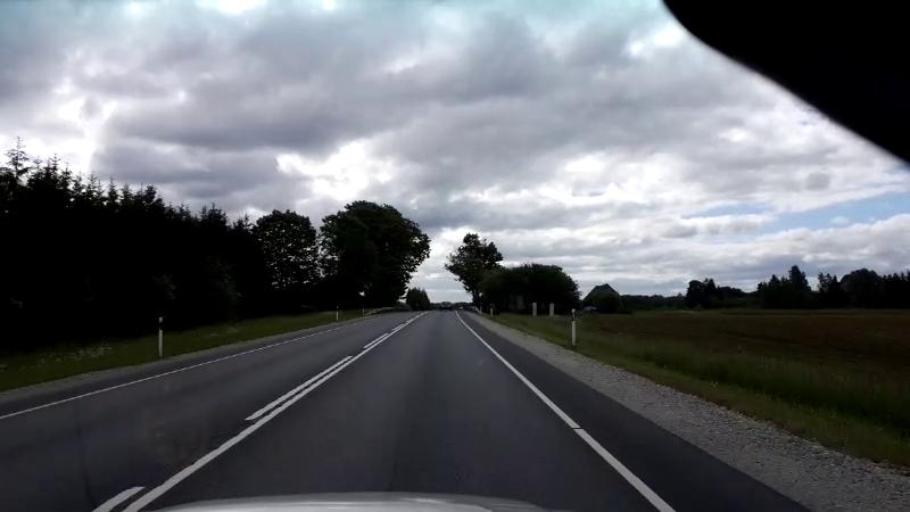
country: EE
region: Paernumaa
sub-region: Halinga vald
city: Parnu-Jaagupi
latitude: 58.6675
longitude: 24.4560
